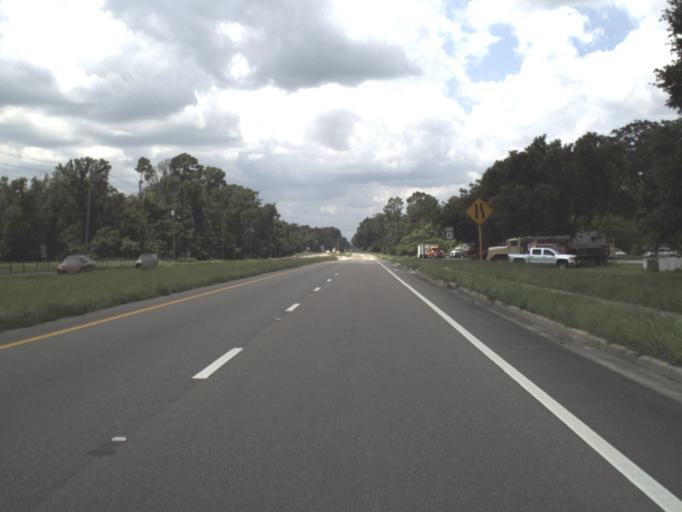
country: US
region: Florida
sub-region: Hernando County
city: Masaryktown
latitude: 28.4512
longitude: -82.4524
